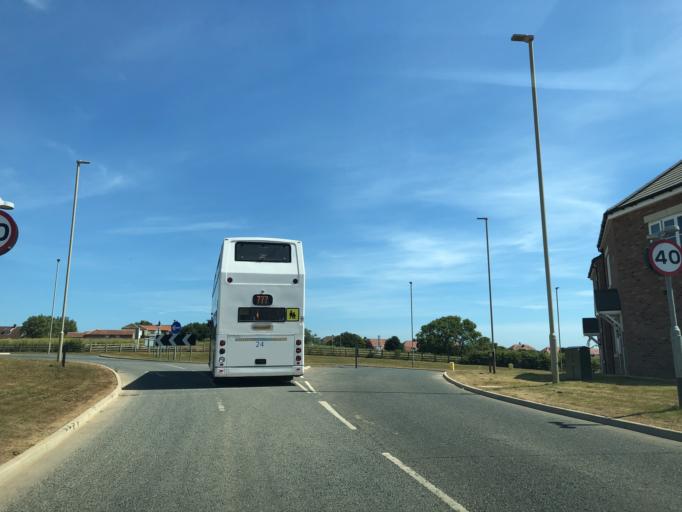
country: GB
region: England
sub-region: North Yorkshire
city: Scarborough
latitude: 54.2475
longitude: -0.3852
